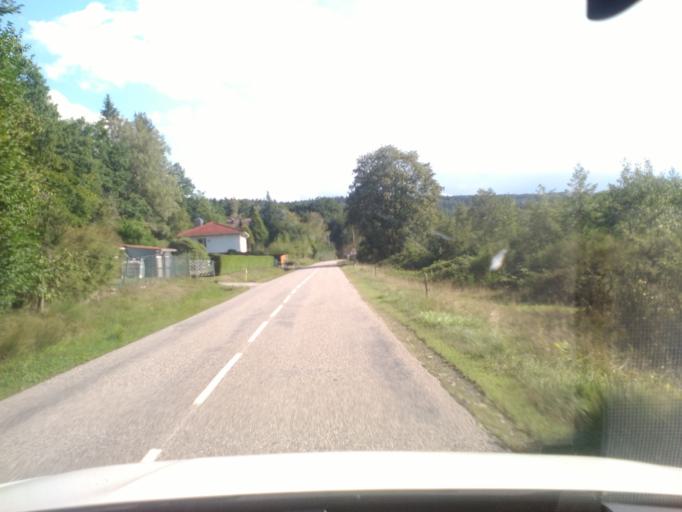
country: FR
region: Lorraine
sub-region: Departement des Vosges
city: Taintrux
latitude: 48.2324
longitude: 6.9043
